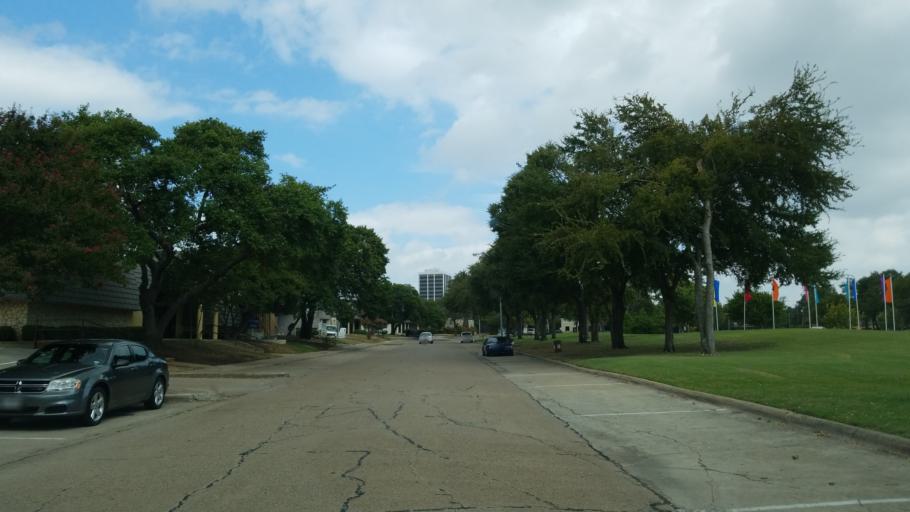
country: US
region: Texas
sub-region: Dallas County
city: Richardson
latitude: 32.9488
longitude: -96.7662
